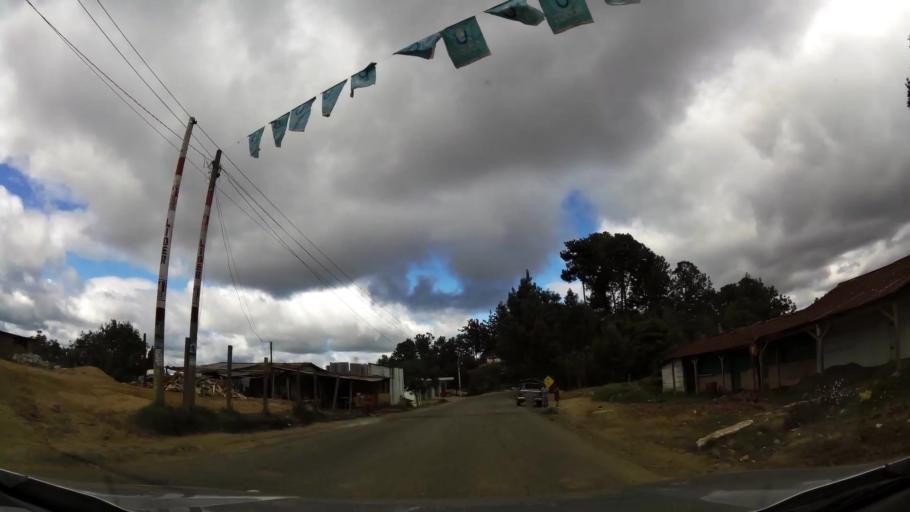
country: GT
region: Quiche
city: Chichicastenango
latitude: 14.8997
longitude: -91.1142
